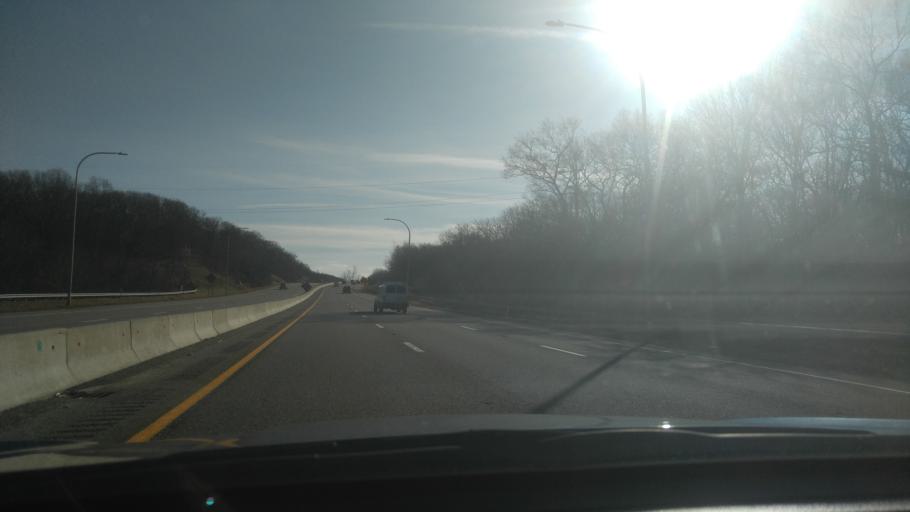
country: US
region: Rhode Island
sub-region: Providence County
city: Cumberland Hill
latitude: 41.9610
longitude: -71.4837
